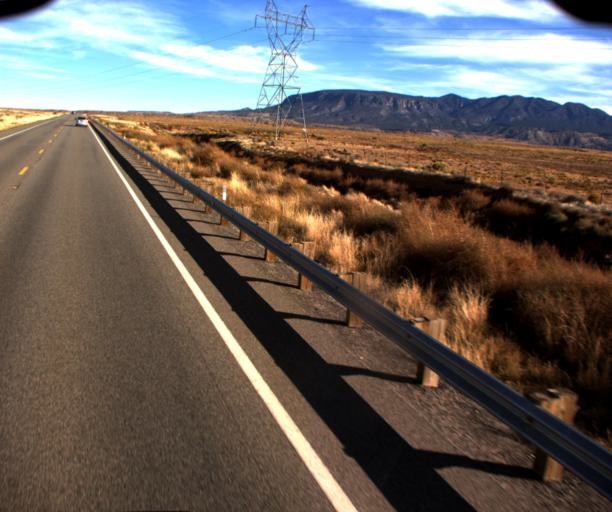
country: US
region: Arizona
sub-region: Apache County
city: Lukachukai
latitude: 36.9374
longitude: -109.2413
